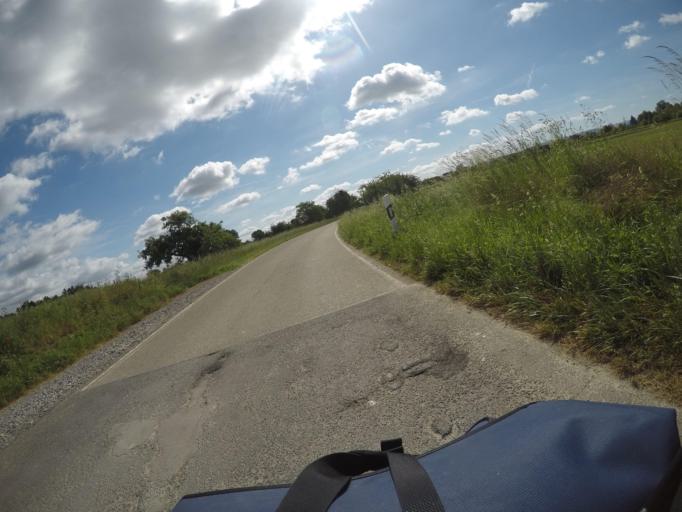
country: DE
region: Baden-Wuerttemberg
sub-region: Karlsruhe Region
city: Au am Rhein
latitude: 48.9555
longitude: 8.2265
